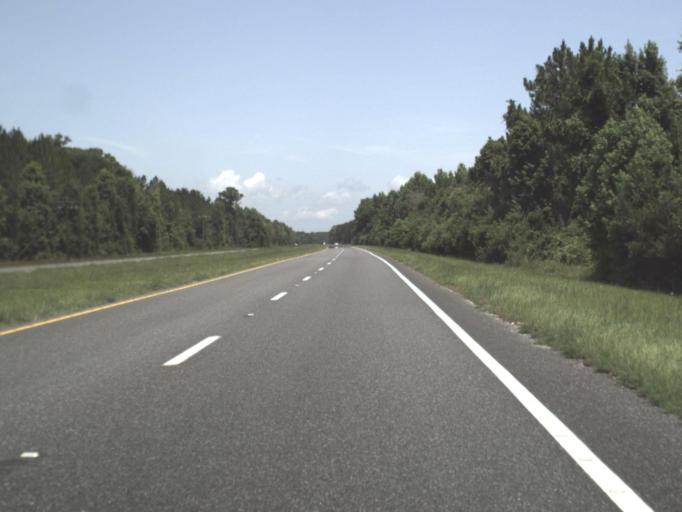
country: US
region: Florida
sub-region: Taylor County
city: Steinhatchee
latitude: 29.8690
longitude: -83.3967
